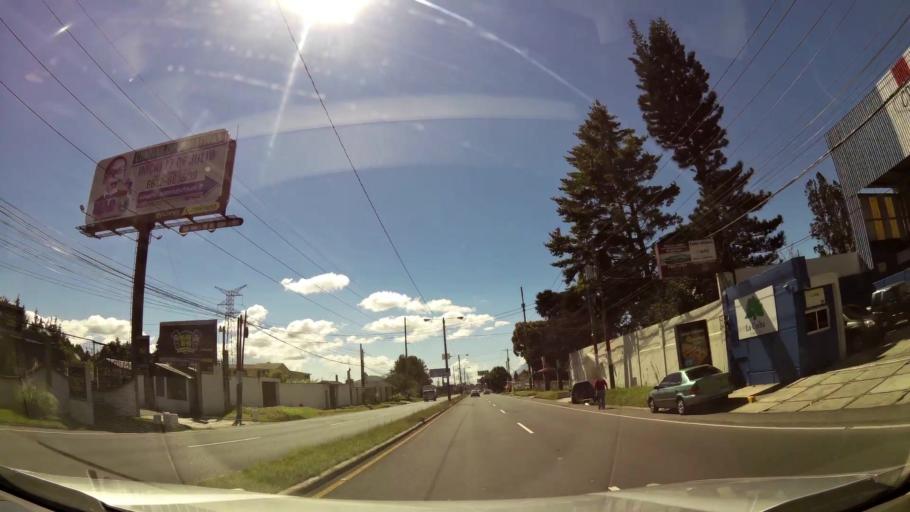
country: GT
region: Guatemala
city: Santa Catarina Pinula
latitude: 14.5216
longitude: -90.4703
